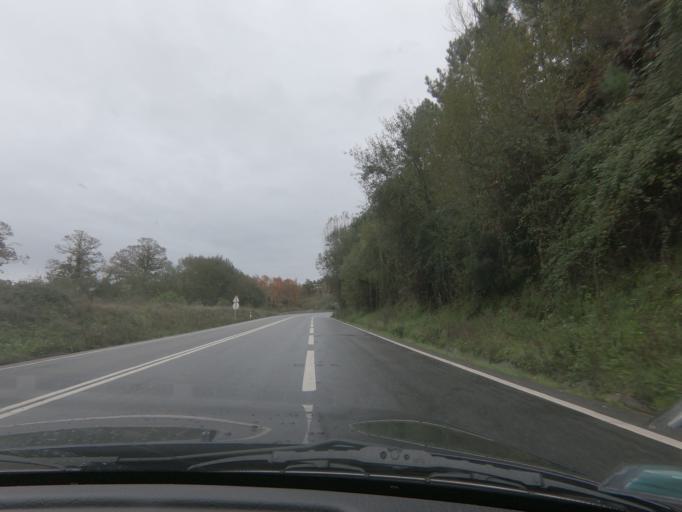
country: PT
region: Porto
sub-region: Amarante
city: Teloes
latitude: 41.3149
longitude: -8.0756
